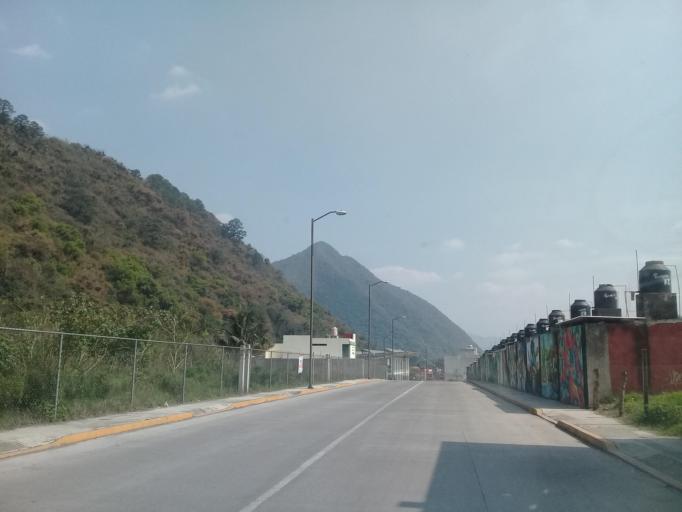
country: MX
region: Veracruz
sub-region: Mariano Escobedo
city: Palmira
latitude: 18.8790
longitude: -97.1026
